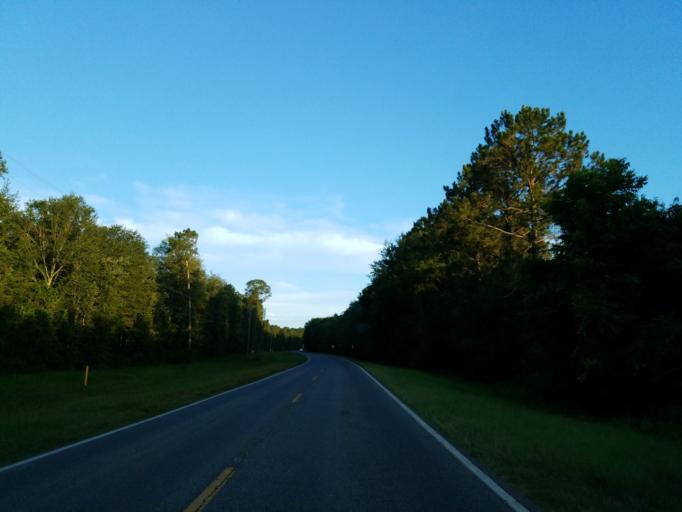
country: US
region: Georgia
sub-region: Cook County
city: Sparks
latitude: 31.2112
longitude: -83.4528
